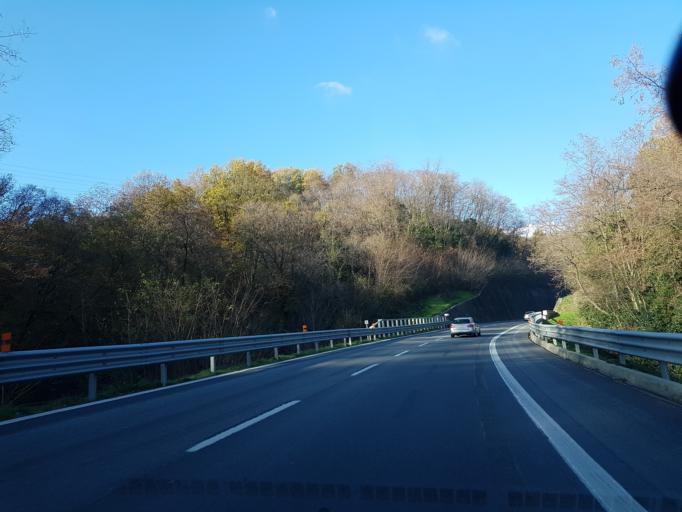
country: IT
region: Liguria
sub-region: Provincia di Genova
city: Manesseno
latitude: 44.4868
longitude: 8.9165
